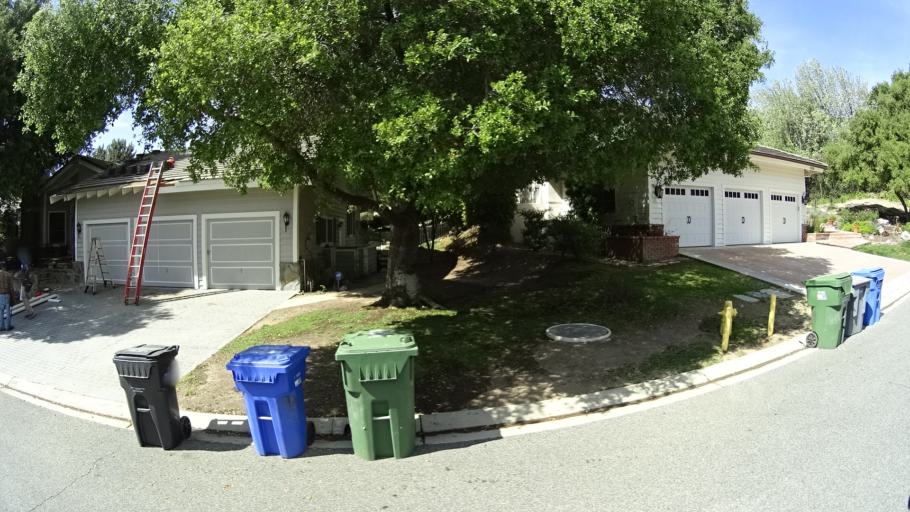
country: US
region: California
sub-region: Los Angeles County
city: Westlake Village
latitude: 34.1692
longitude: -118.7907
